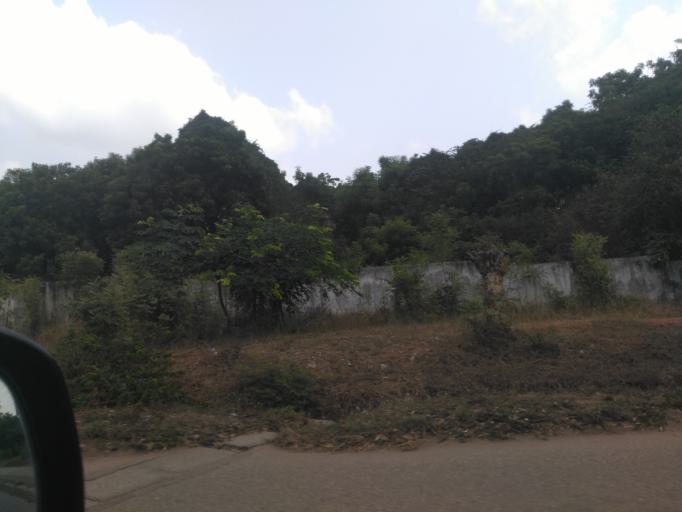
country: GH
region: Greater Accra
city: Accra
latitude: 5.5971
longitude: -0.1915
